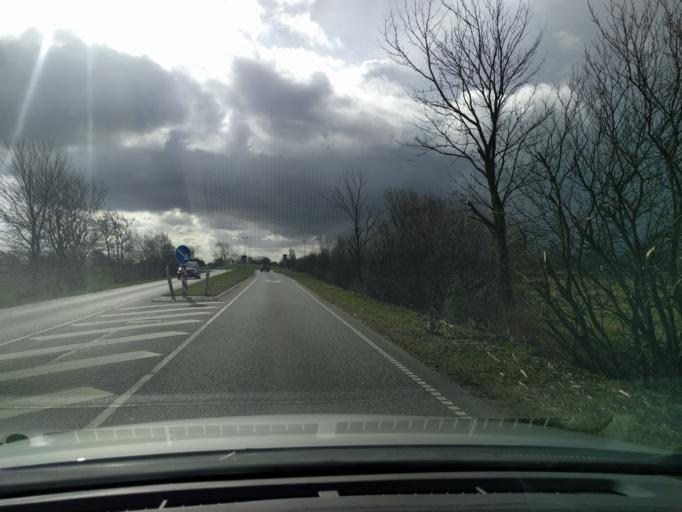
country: DK
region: South Denmark
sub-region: Kolding Kommune
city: Vamdrup
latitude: 55.4297
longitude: 9.3055
